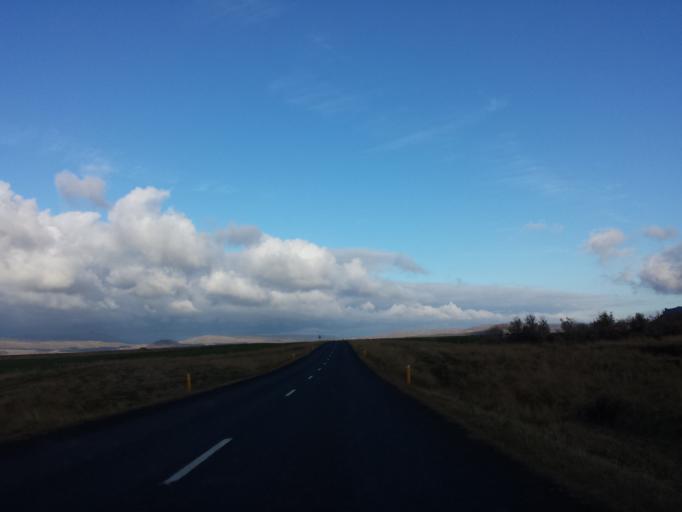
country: IS
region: West
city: Borgarnes
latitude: 64.8047
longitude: -22.2634
